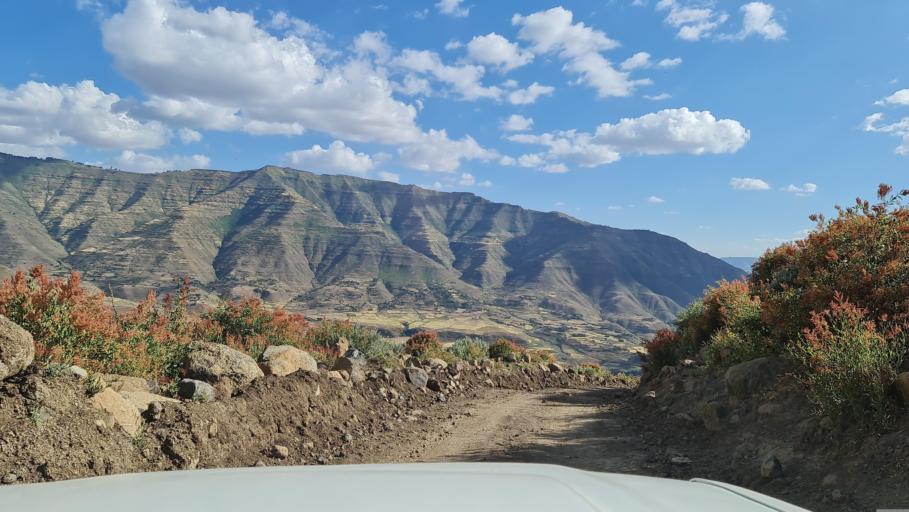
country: ET
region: Amhara
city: Debark'
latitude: 13.1230
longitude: 38.0209
